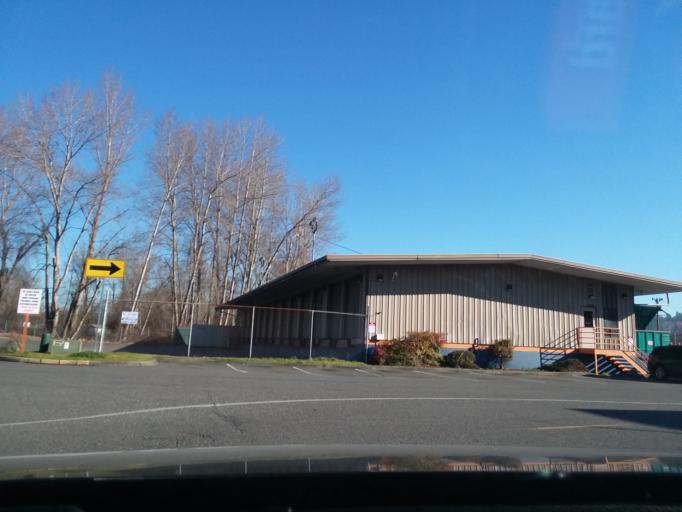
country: US
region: Washington
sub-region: Pierce County
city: Fife
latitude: 47.2443
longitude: -122.3705
